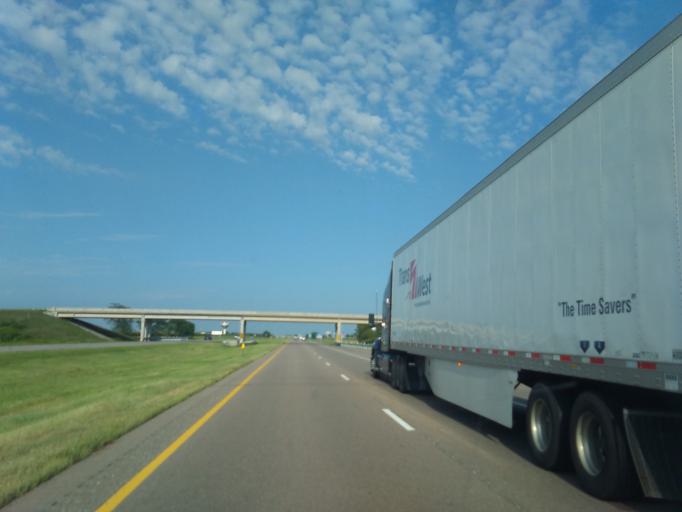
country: US
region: Nebraska
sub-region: York County
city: York
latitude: 40.8212
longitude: -97.6183
